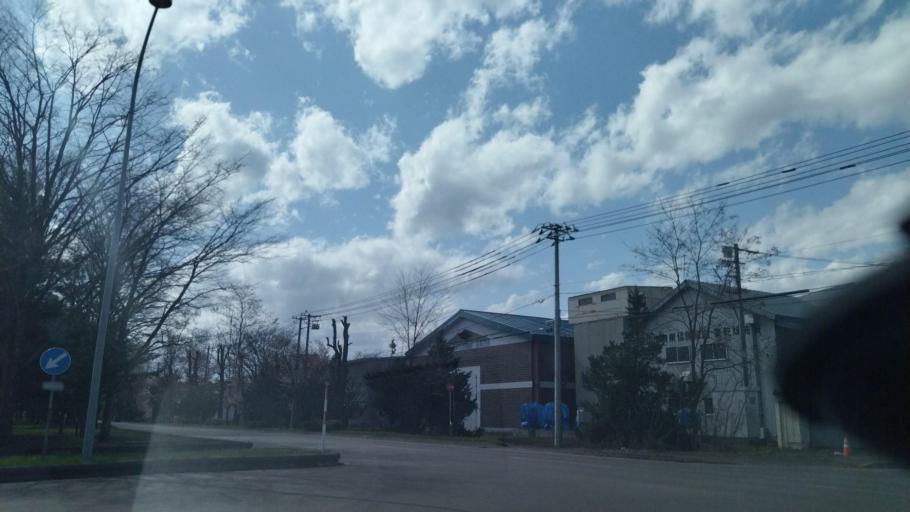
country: JP
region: Hokkaido
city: Obihiro
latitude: 42.9297
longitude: 143.1357
